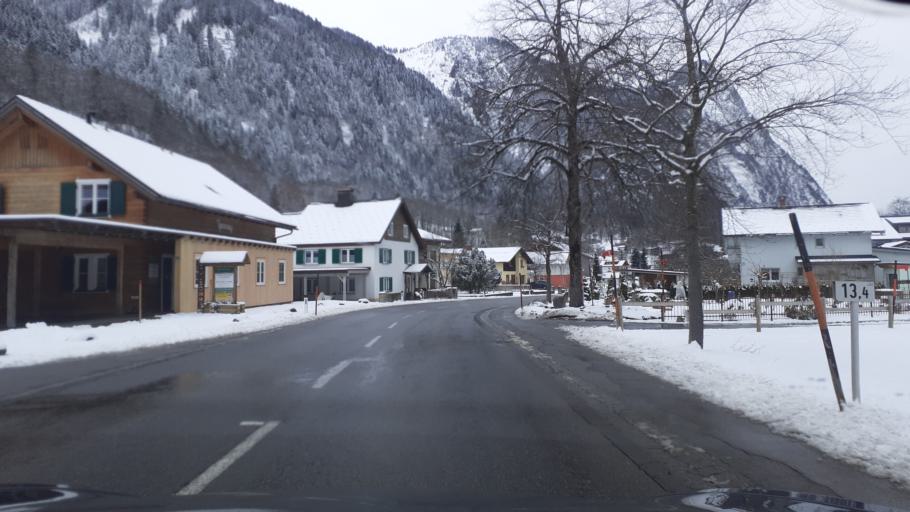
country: AT
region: Vorarlberg
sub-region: Politischer Bezirk Bludenz
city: Dalaas
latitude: 47.1222
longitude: 9.9951
